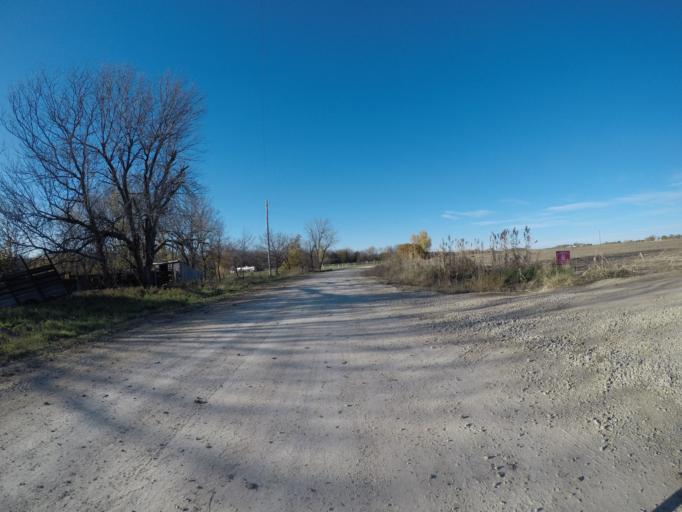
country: US
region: Kansas
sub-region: Riley County
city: Fort Riley North
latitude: 39.2680
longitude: -96.7840
